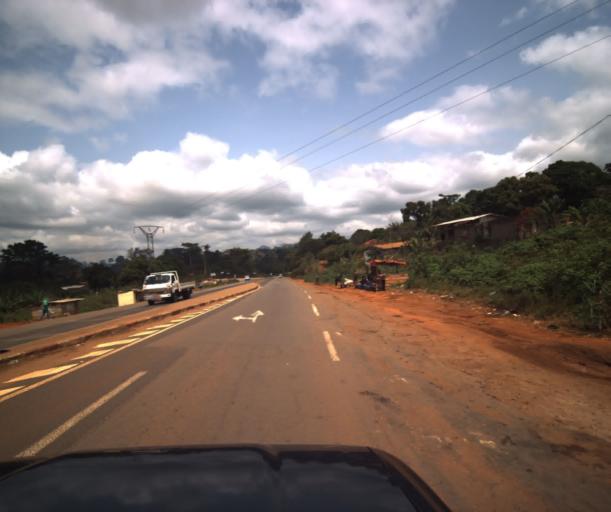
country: CM
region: Centre
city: Mbankomo
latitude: 3.7889
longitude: 11.4225
